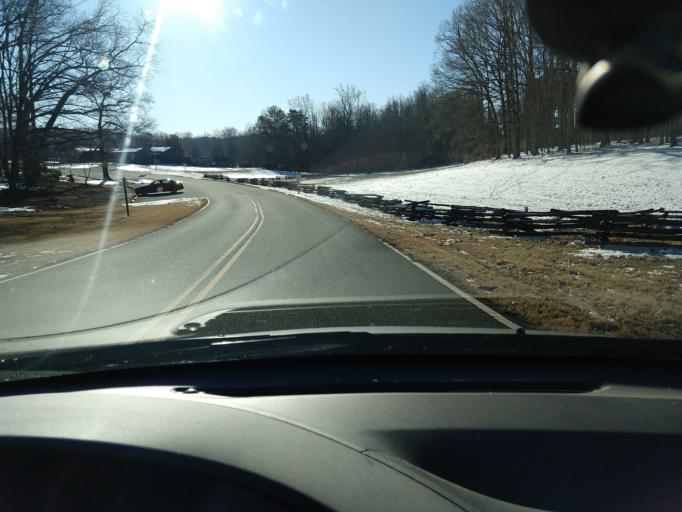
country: US
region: Virginia
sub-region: Franklin County
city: North Shore
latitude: 37.1205
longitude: -79.7333
